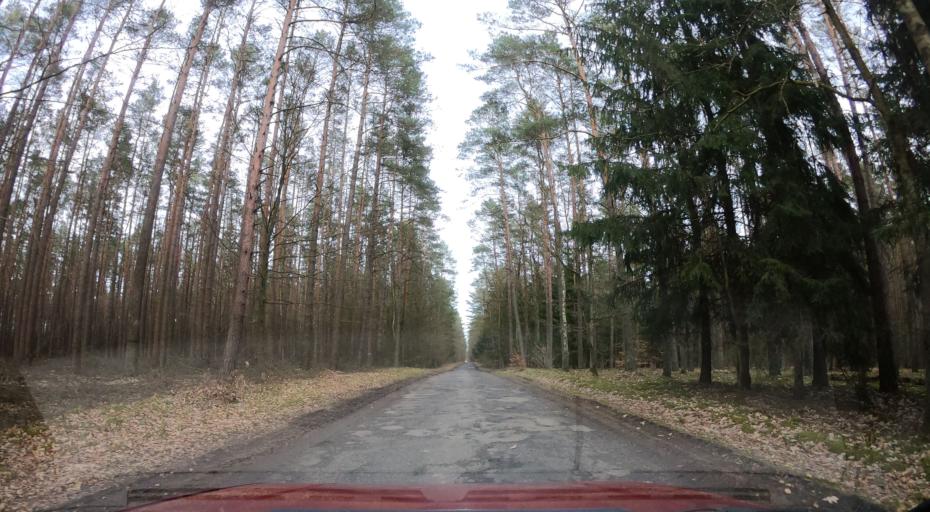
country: PL
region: West Pomeranian Voivodeship
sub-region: Powiat mysliborski
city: Mysliborz
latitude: 52.8883
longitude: 14.7307
